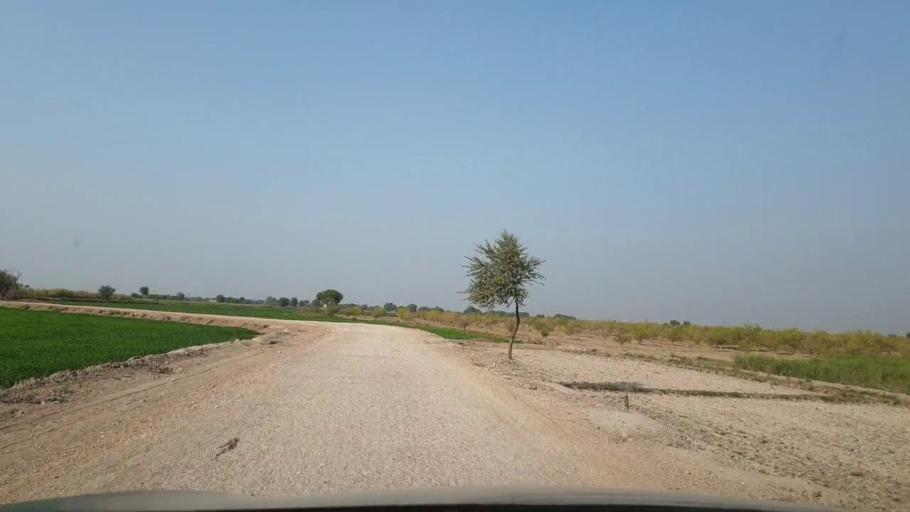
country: PK
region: Sindh
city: Tando Allahyar
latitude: 25.5762
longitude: 68.7951
